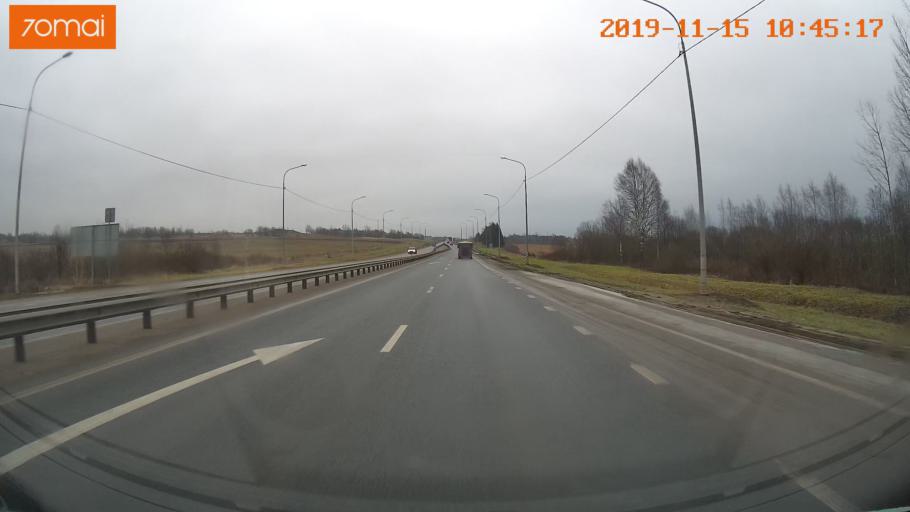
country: RU
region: Vologda
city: Sheksna
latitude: 59.2109
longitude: 38.5833
